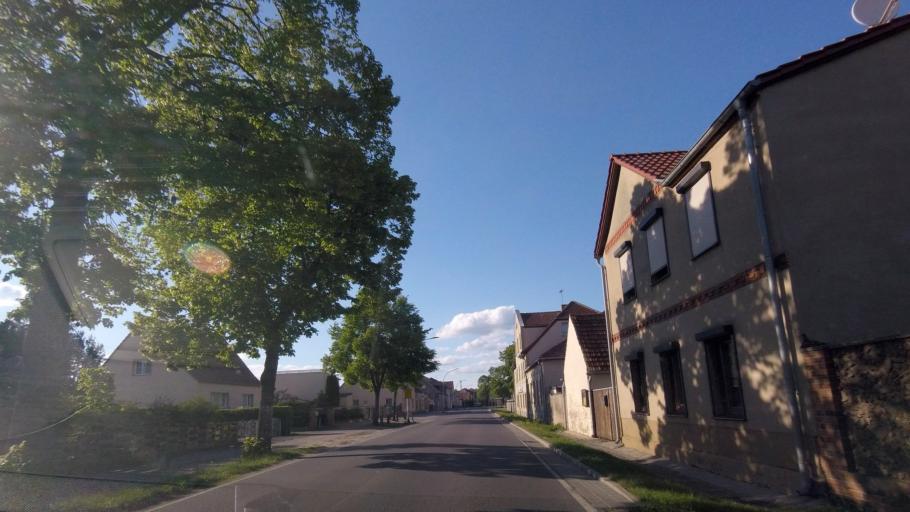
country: DE
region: Brandenburg
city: Luebben
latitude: 51.9319
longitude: 13.8925
